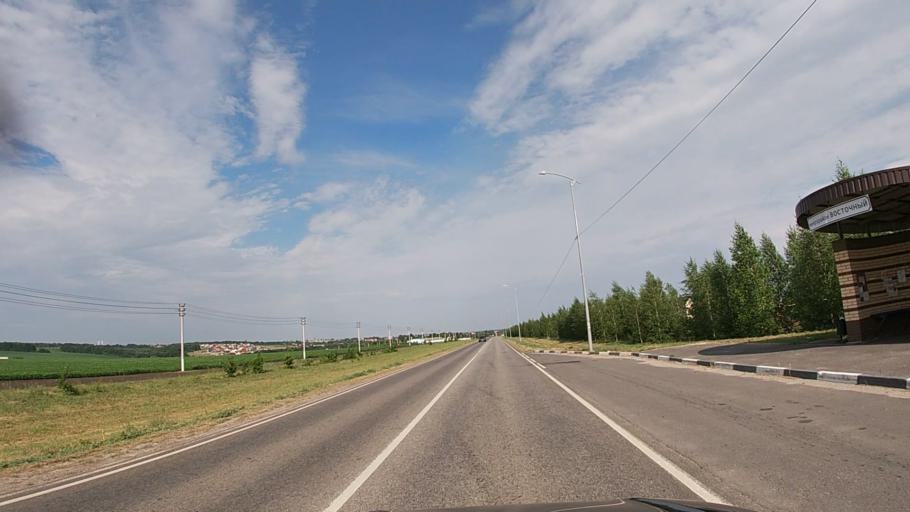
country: RU
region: Belgorod
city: Krasnaya Yaruga
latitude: 50.7970
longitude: 35.6889
